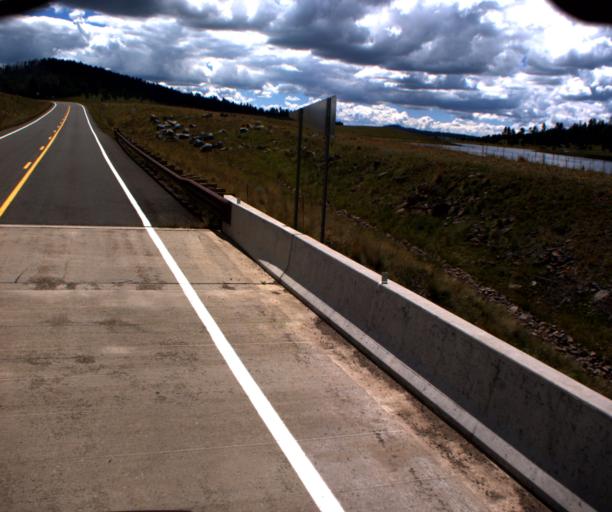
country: US
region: Arizona
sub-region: Apache County
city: Eagar
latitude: 33.9172
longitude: -109.4247
